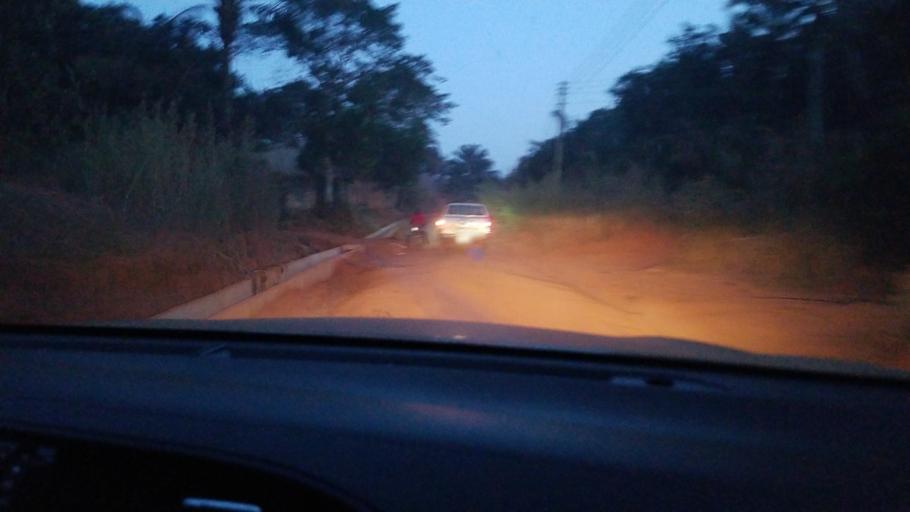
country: NG
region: Enugu
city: Obollo-Afor
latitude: 6.9027
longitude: 7.5104
